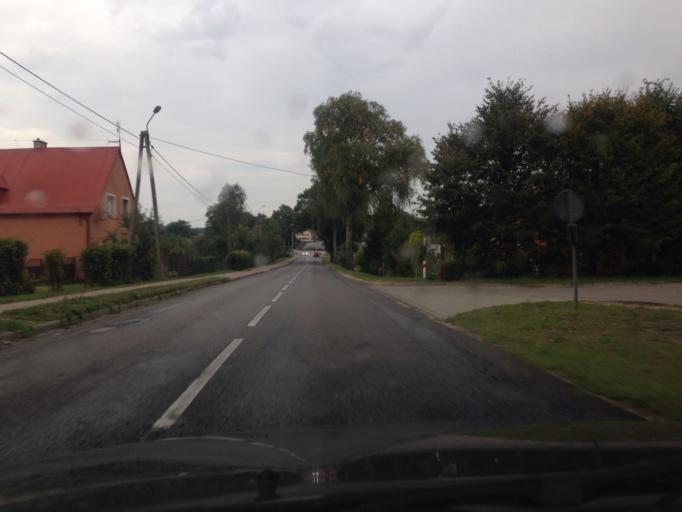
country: PL
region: Pomeranian Voivodeship
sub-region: Powiat bytowski
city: Czarna Dabrowka
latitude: 54.3570
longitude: 17.5593
